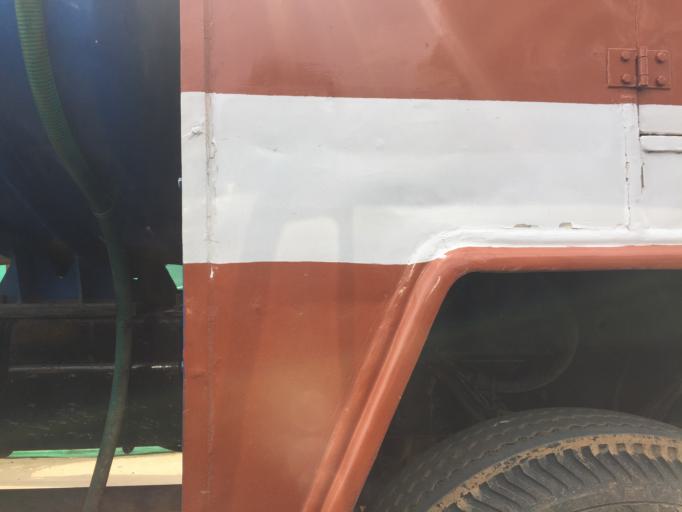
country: IN
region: Karnataka
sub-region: Bangalore Rural
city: Hoskote
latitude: 12.9777
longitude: 77.7273
